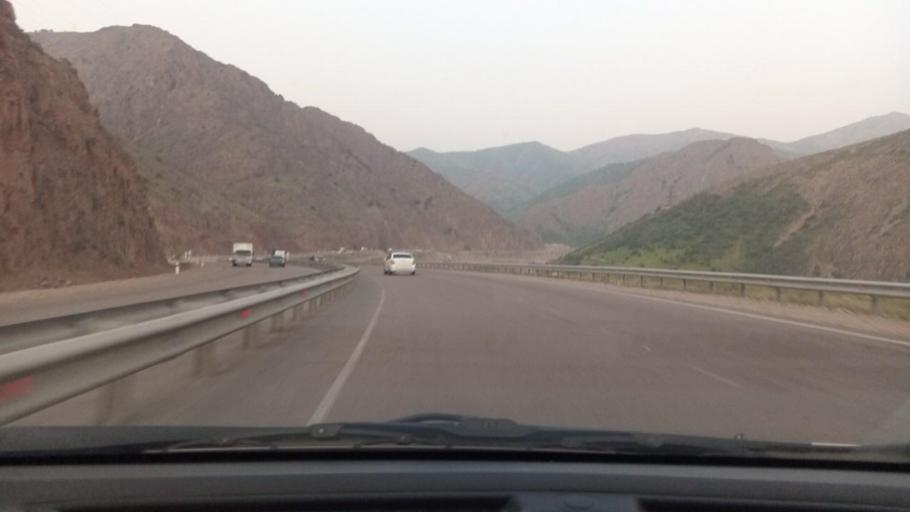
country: UZ
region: Toshkent
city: Angren
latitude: 41.0752
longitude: 70.2919
